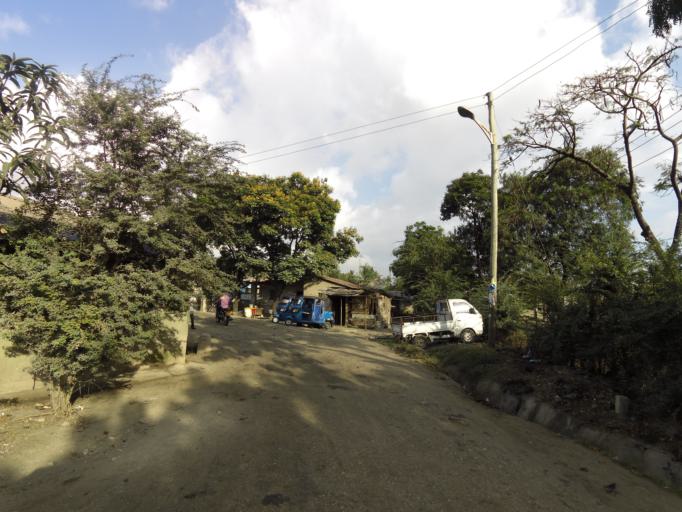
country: TZ
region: Dar es Salaam
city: Magomeni
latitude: -6.7914
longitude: 39.2295
